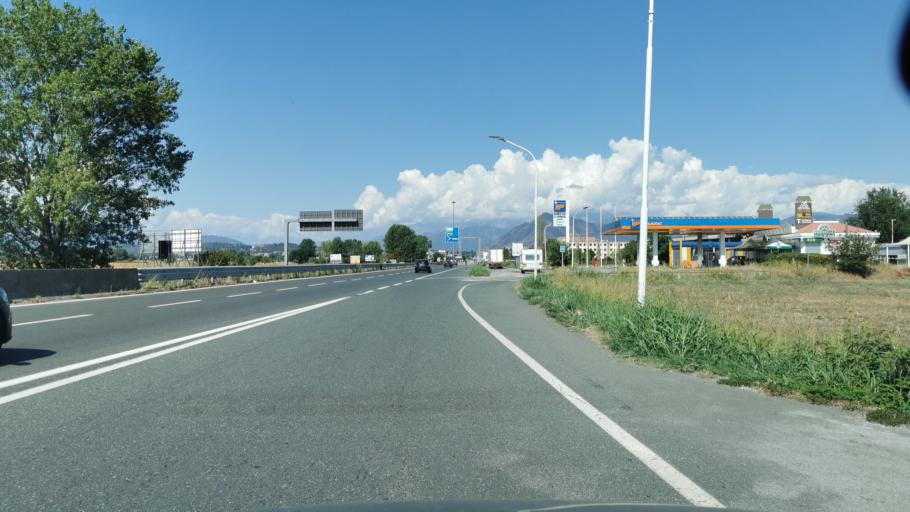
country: IT
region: Piedmont
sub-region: Provincia di Torino
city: Grugliasco
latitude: 45.0553
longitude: 7.5642
